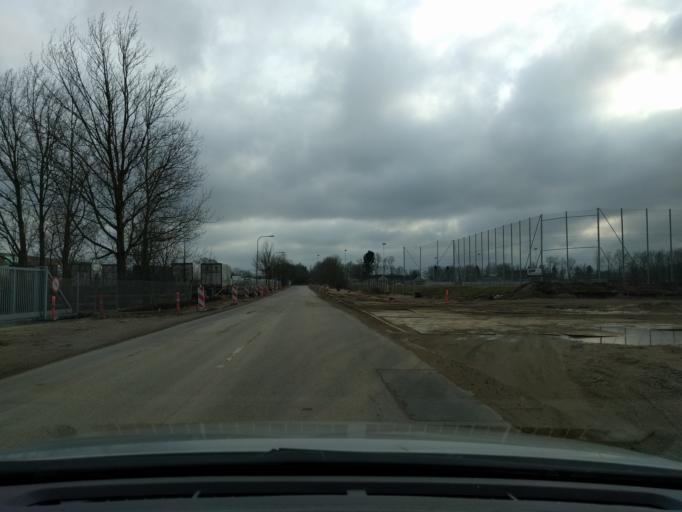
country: DK
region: South Denmark
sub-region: Odense Kommune
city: Bellinge
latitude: 55.3617
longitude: 10.3247
